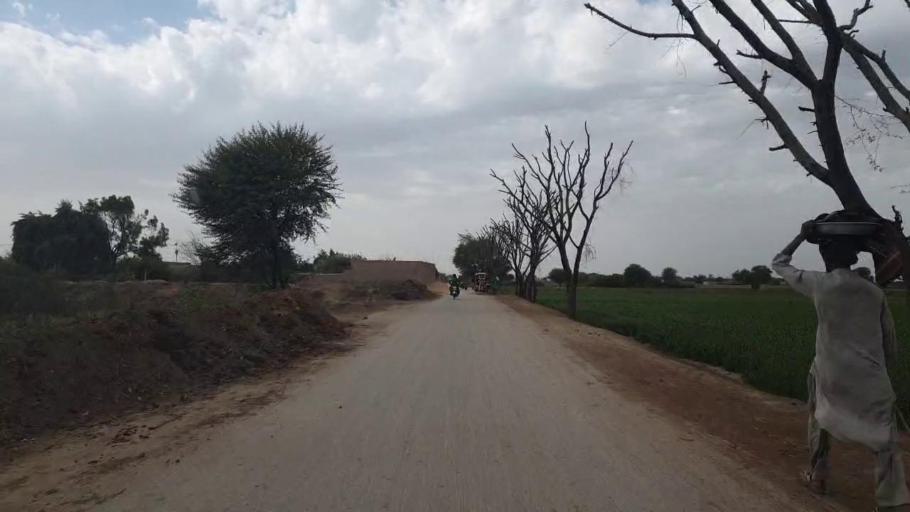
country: PK
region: Sindh
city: Hala
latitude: 25.9359
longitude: 68.4151
